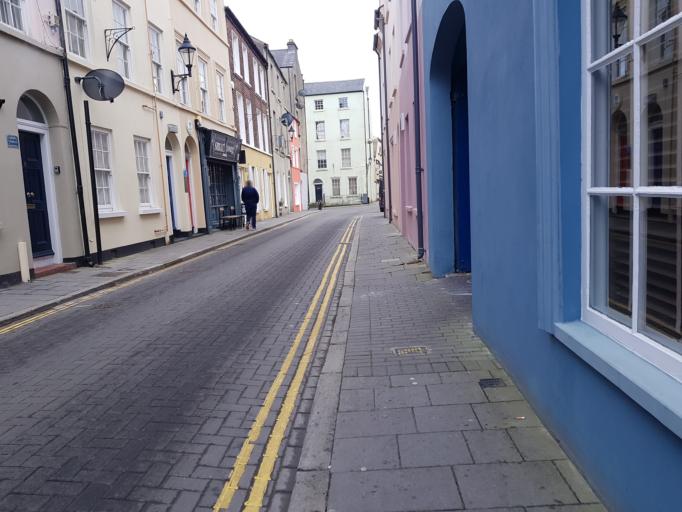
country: GB
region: Northern Ireland
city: Londonderry County Borough
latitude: 54.9947
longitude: -7.3228
